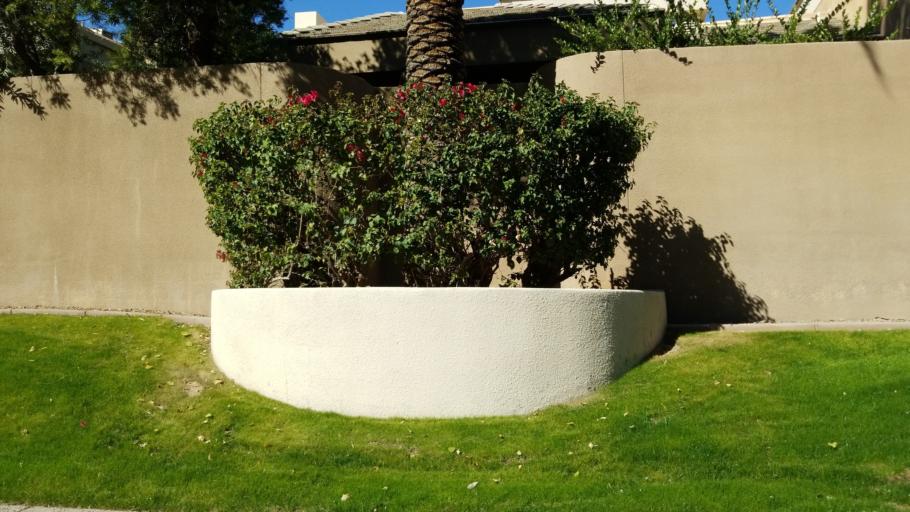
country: US
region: Arizona
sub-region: Maricopa County
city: Paradise Valley
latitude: 33.5683
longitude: -111.9194
